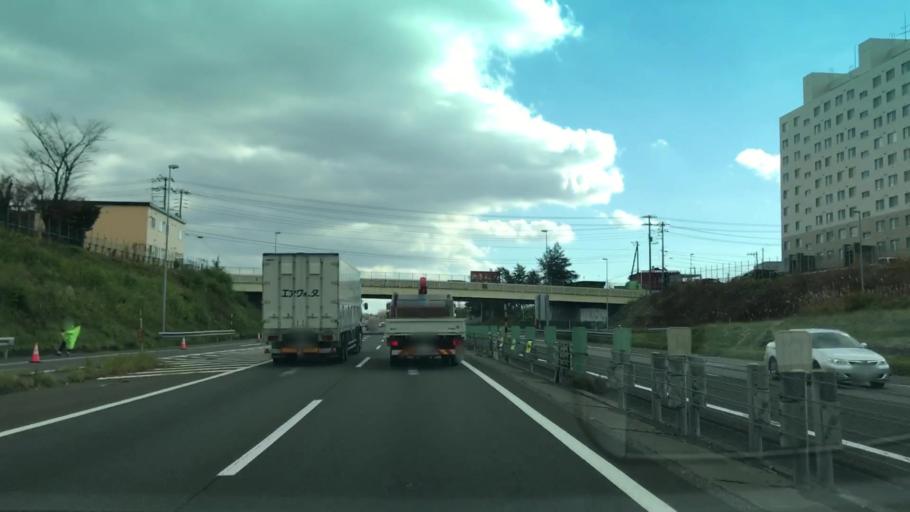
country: JP
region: Hokkaido
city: Kitahiroshima
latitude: 42.9765
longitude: 141.4788
